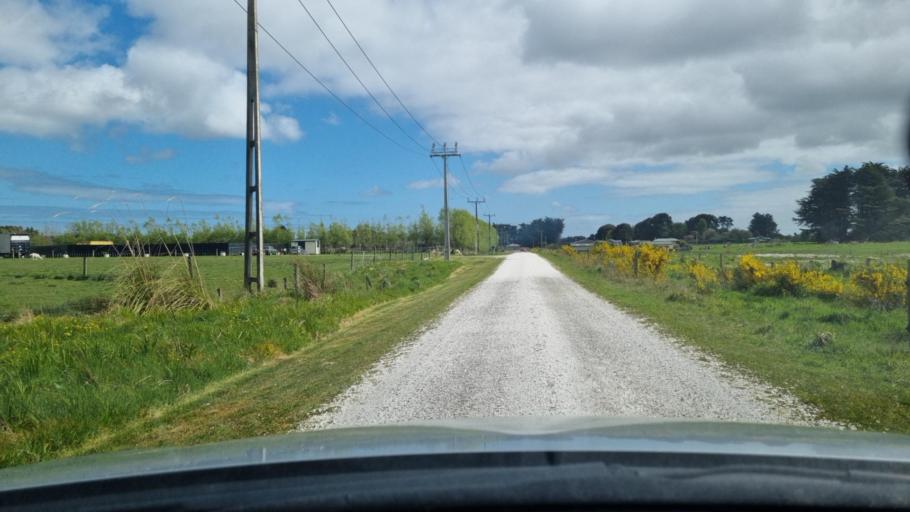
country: NZ
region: Southland
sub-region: Invercargill City
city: Invercargill
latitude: -46.4432
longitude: 168.3870
